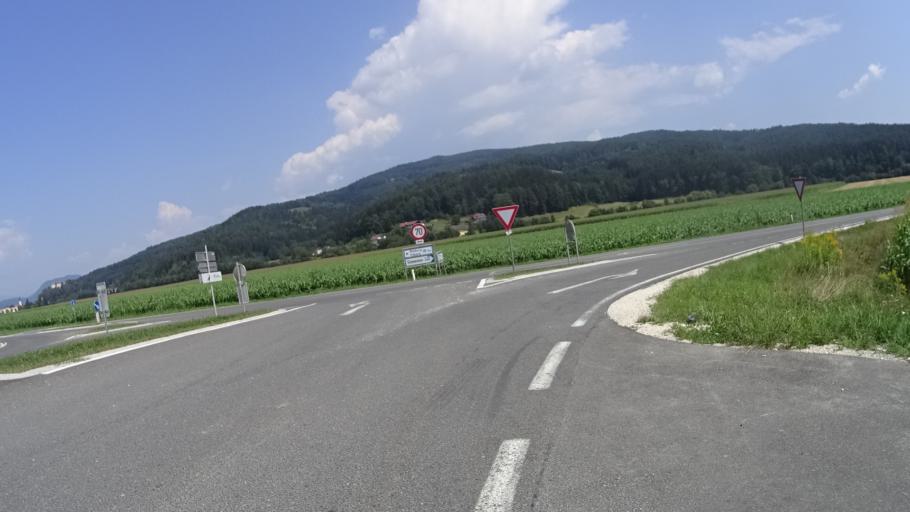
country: AT
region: Carinthia
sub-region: Politischer Bezirk Volkermarkt
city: Bleiburg/Pliberk
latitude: 46.5716
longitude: 14.8034
